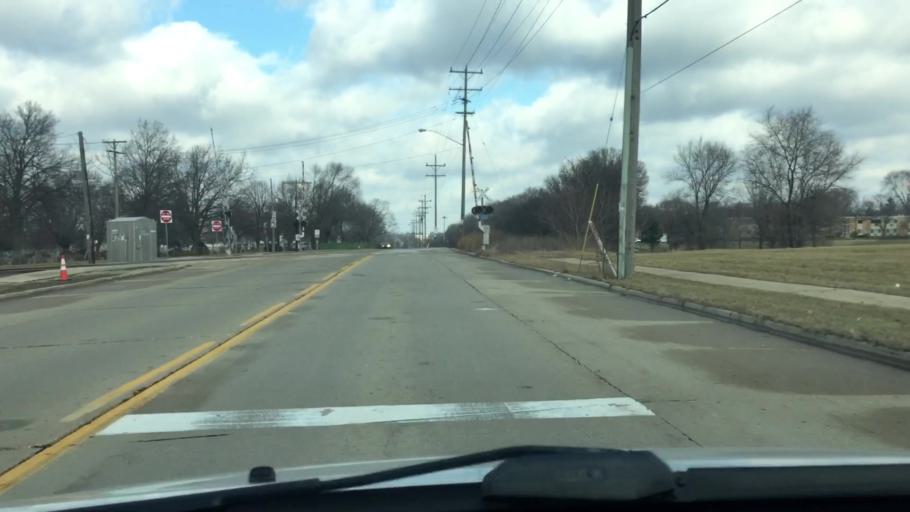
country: US
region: Wisconsin
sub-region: Waukesha County
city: Waukesha
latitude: 42.9932
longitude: -88.2368
